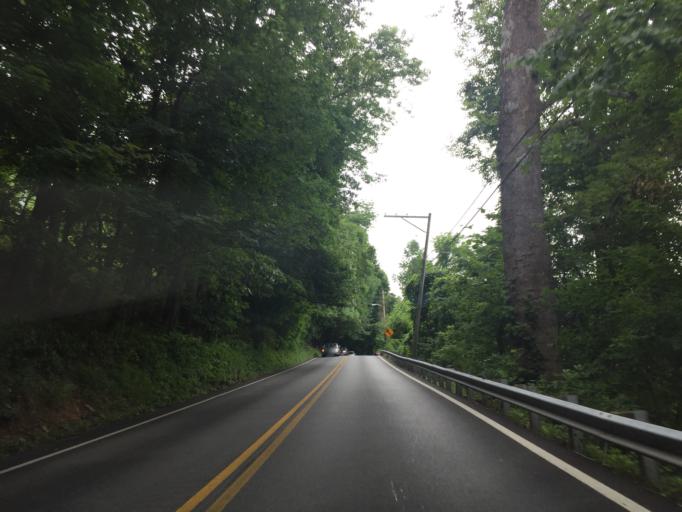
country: US
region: Maryland
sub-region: Baltimore County
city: Carney
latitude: 39.4194
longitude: -76.5398
